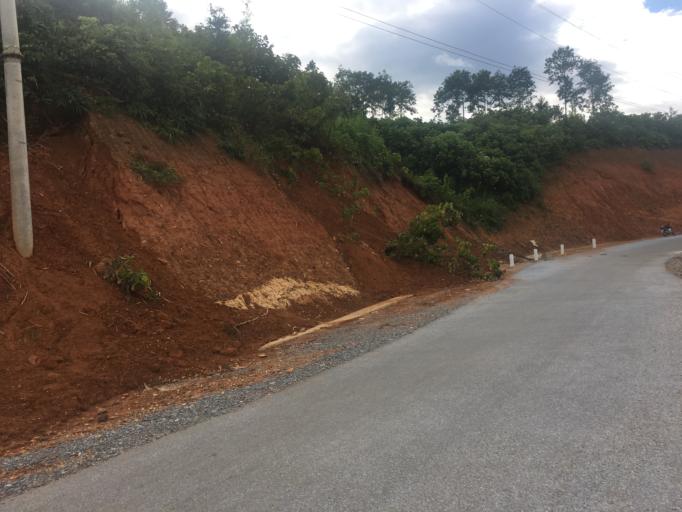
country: VN
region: Ha Giang
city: Thanh Pho Ha Giang
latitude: 22.8829
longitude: 105.0339
